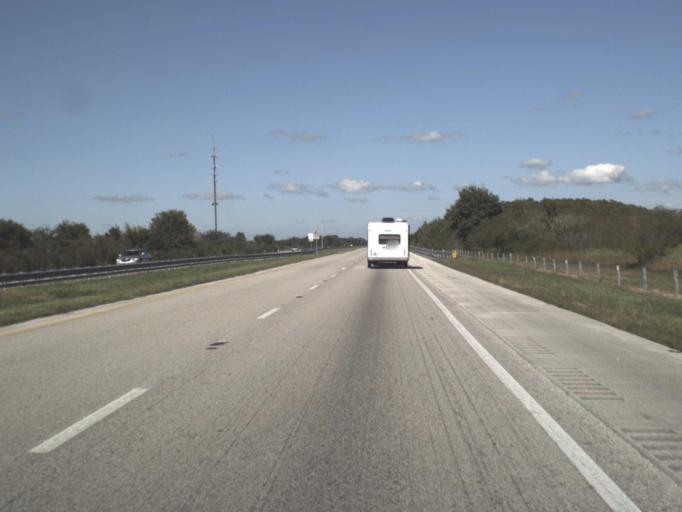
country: US
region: Florida
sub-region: Osceola County
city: Saint Cloud
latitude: 28.0213
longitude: -81.1810
